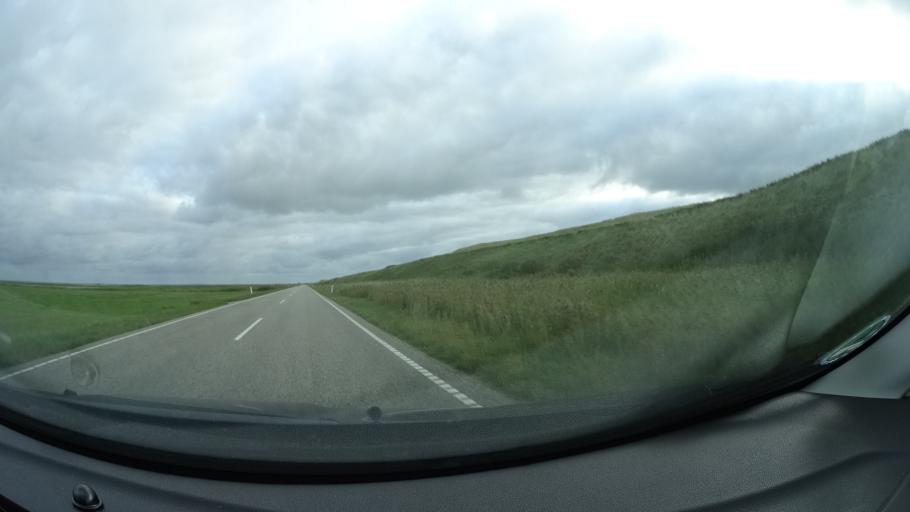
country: DK
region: Central Jutland
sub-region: Lemvig Kommune
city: Harboore
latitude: 56.4098
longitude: 8.1224
